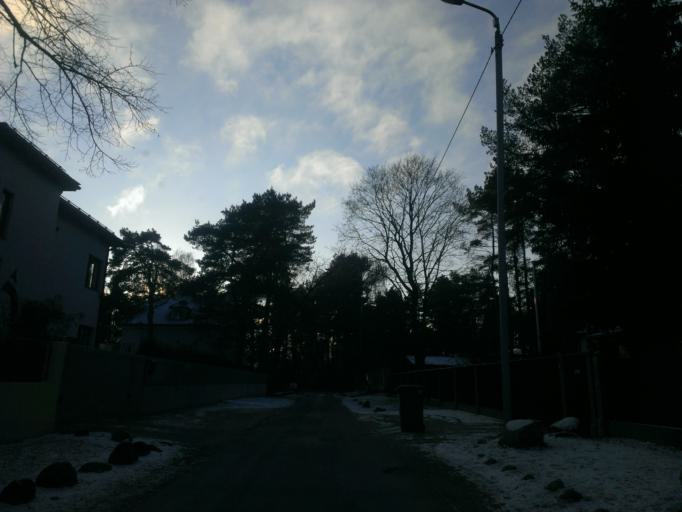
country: LV
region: Riga
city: Jaunciems
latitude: 57.0038
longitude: 24.1636
